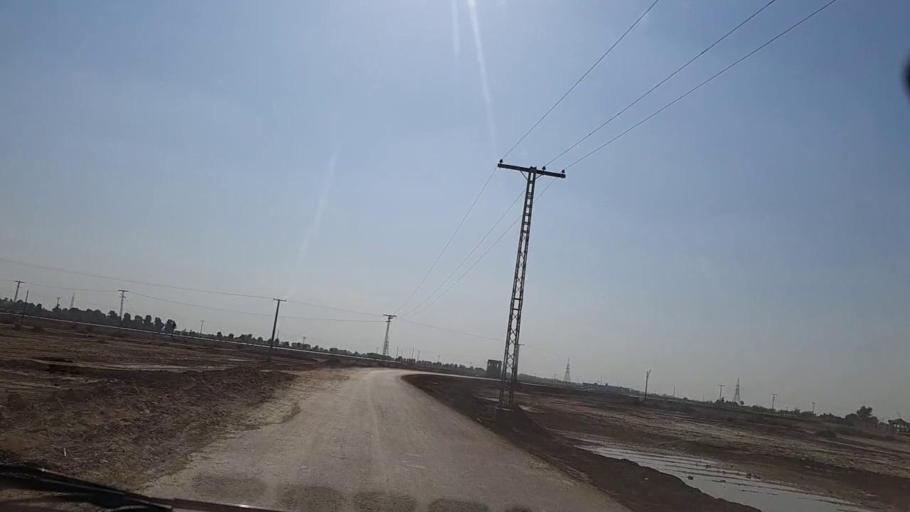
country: PK
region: Sindh
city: Mirpur Khas
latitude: 25.5172
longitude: 68.9526
